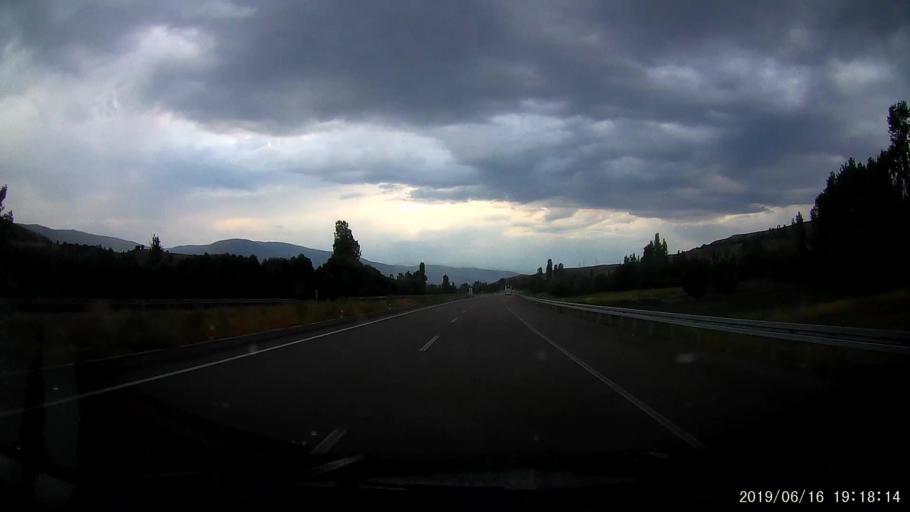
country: TR
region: Sivas
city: Akincilar
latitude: 40.0950
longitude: 38.4637
